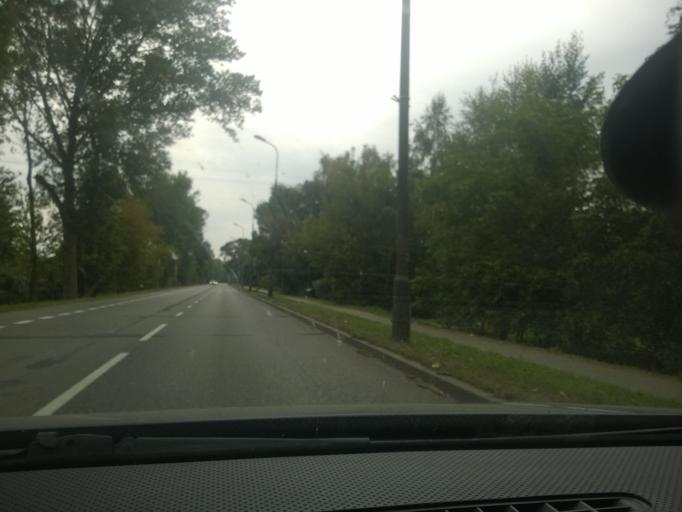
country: PL
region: Masovian Voivodeship
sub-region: Powiat pruszkowski
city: Pruszkow
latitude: 52.1761
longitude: 20.7948
